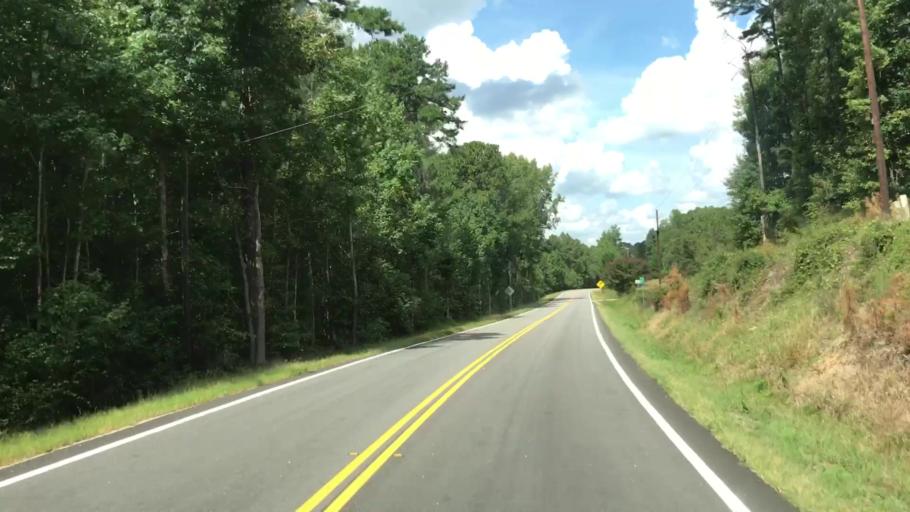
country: US
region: Georgia
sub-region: Greene County
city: Union Point
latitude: 33.5403
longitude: -83.0917
